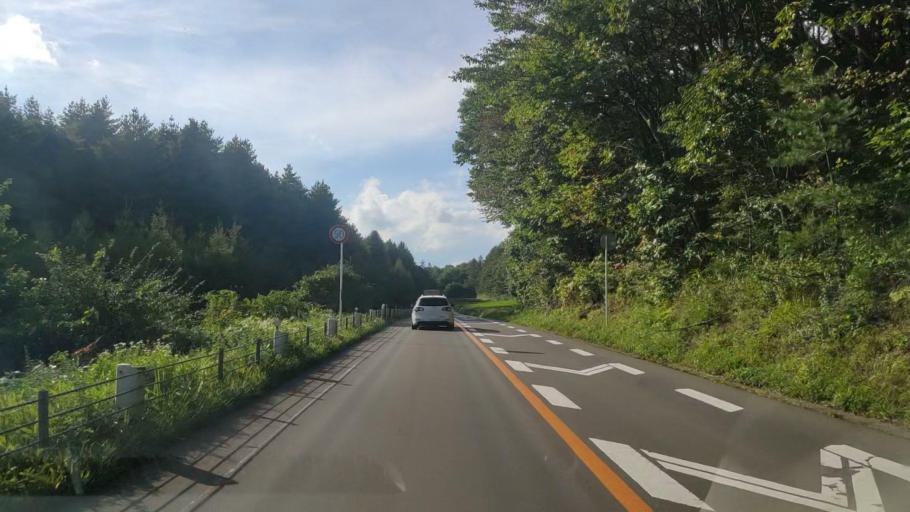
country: JP
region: Nagano
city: Ueda
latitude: 36.4857
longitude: 138.4268
